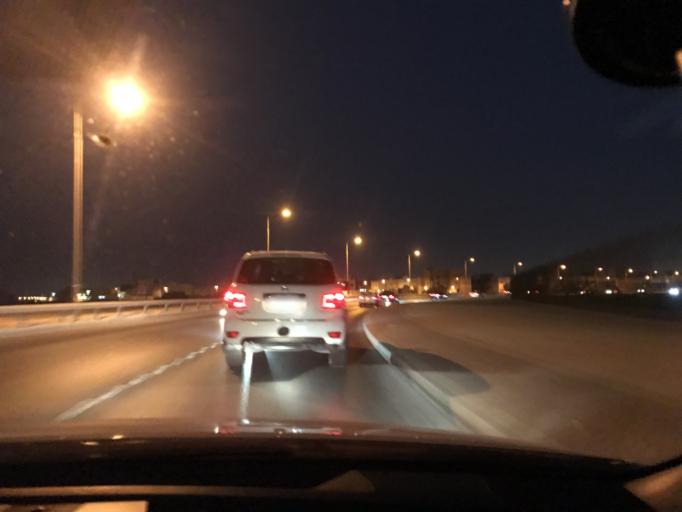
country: BH
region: Muharraq
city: Al Muharraq
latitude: 26.2831
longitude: 50.6139
